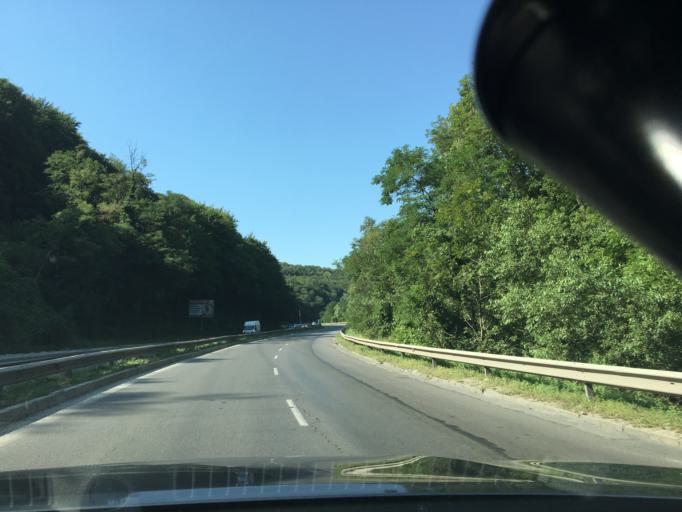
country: BG
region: Sofiya
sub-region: Obshtina Bozhurishte
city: Bozhurishte
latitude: 42.6391
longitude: 23.1986
